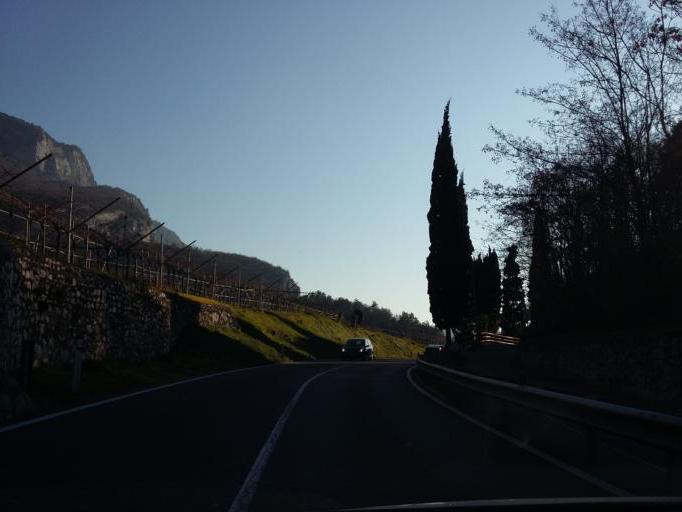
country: IT
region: Trentino-Alto Adige
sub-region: Provincia di Trento
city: Nago-Torbole
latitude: 45.8765
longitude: 10.9044
